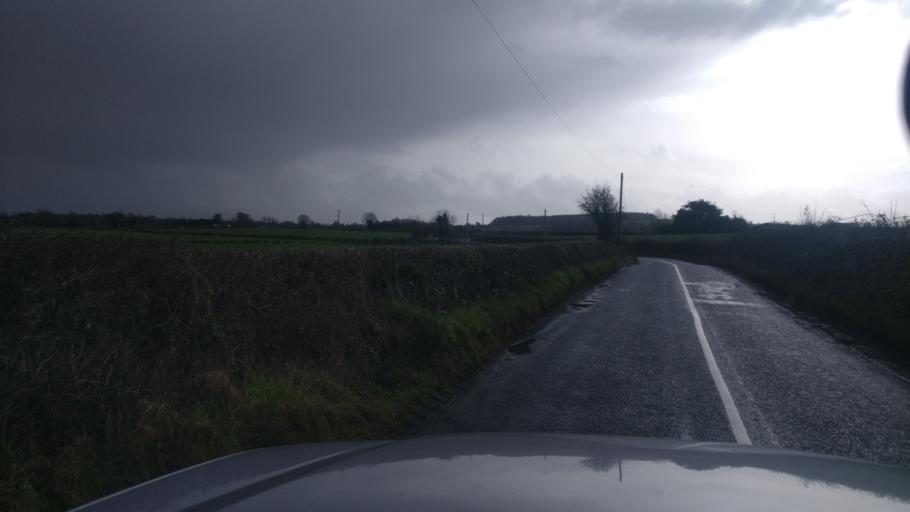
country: IE
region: Munster
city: Nenagh Bridge
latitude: 52.9635
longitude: -8.0842
